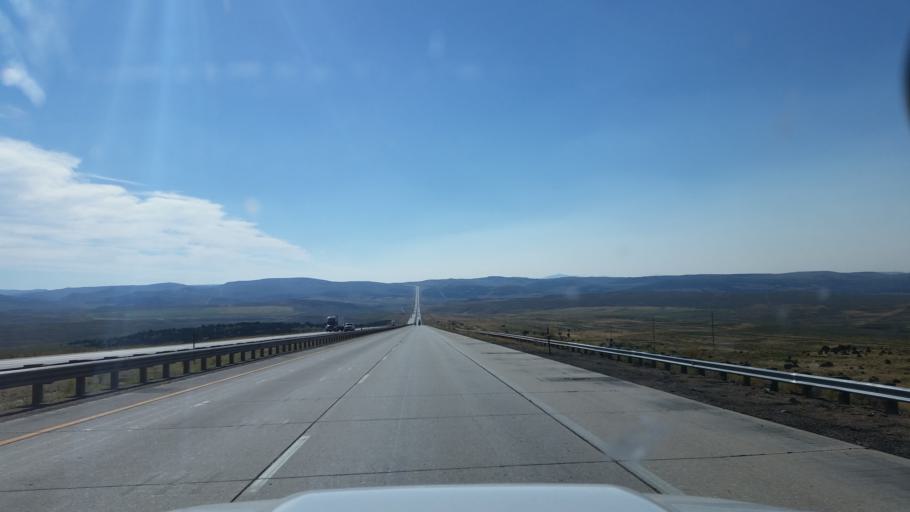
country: US
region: Wyoming
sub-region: Uinta County
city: Mountain View
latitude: 41.2975
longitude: -110.5657
